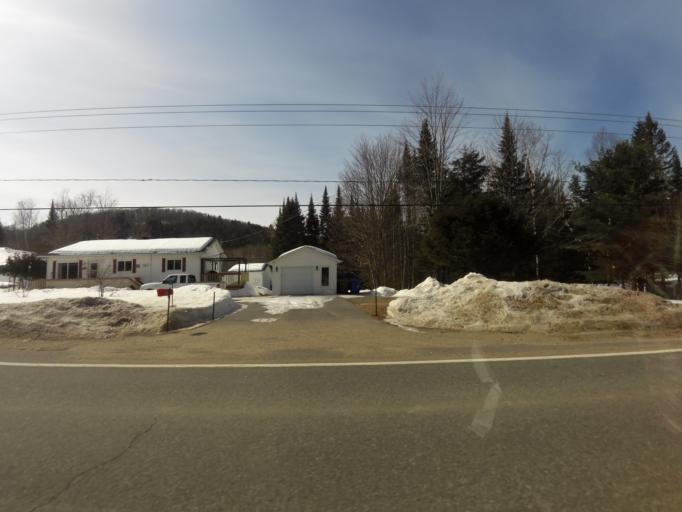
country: CA
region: Quebec
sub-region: Outaouais
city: Val-des-Monts
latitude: 45.8797
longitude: -75.6009
